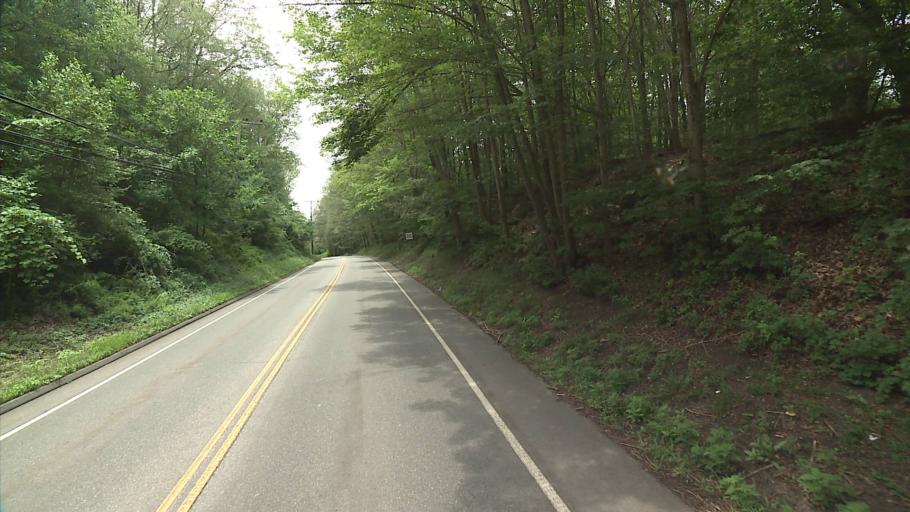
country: US
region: Connecticut
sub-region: New Haven County
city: Guilford
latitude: 41.3568
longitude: -72.6512
